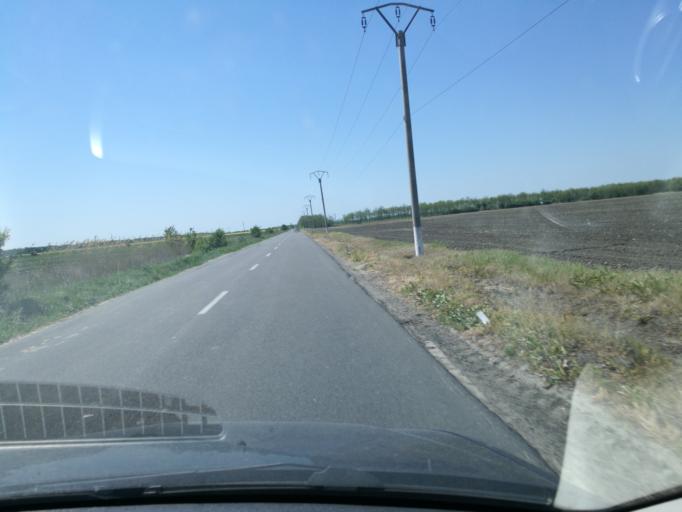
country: RO
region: Prahova
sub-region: Comuna Draganesti
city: Meri
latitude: 44.8461
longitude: 26.3251
